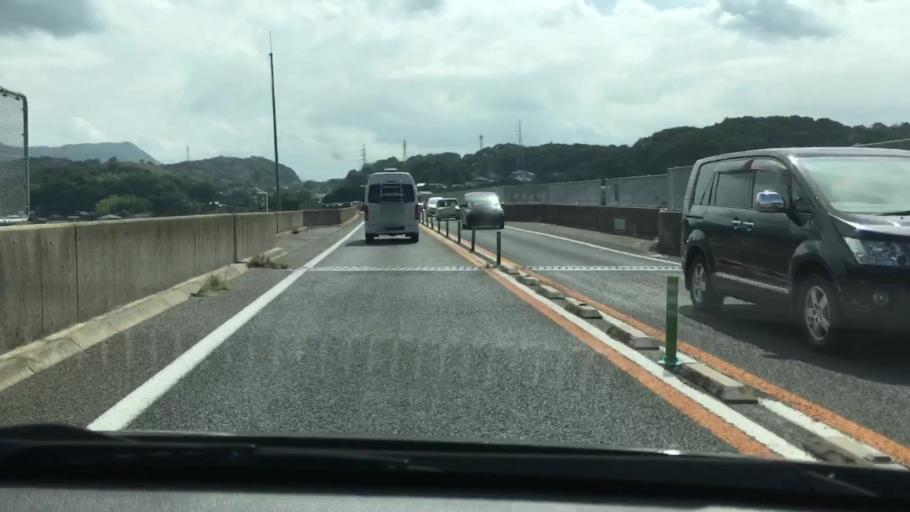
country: JP
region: Nagasaki
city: Sasebo
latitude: 33.1508
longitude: 129.7467
